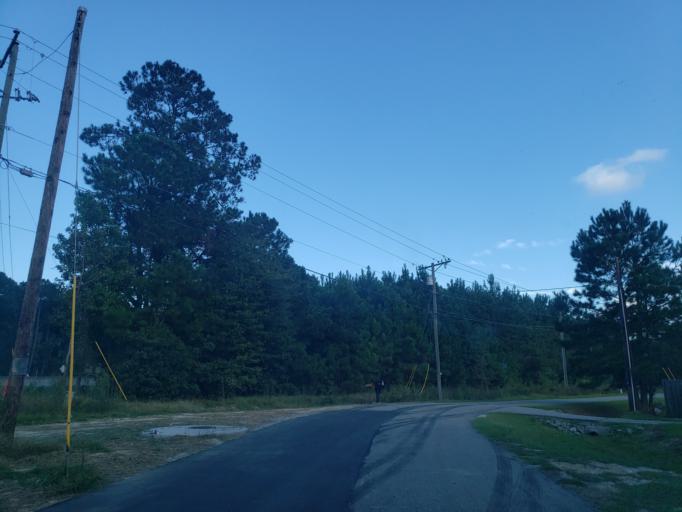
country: US
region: Georgia
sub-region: Chatham County
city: Georgetown
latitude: 31.9976
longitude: -81.2440
